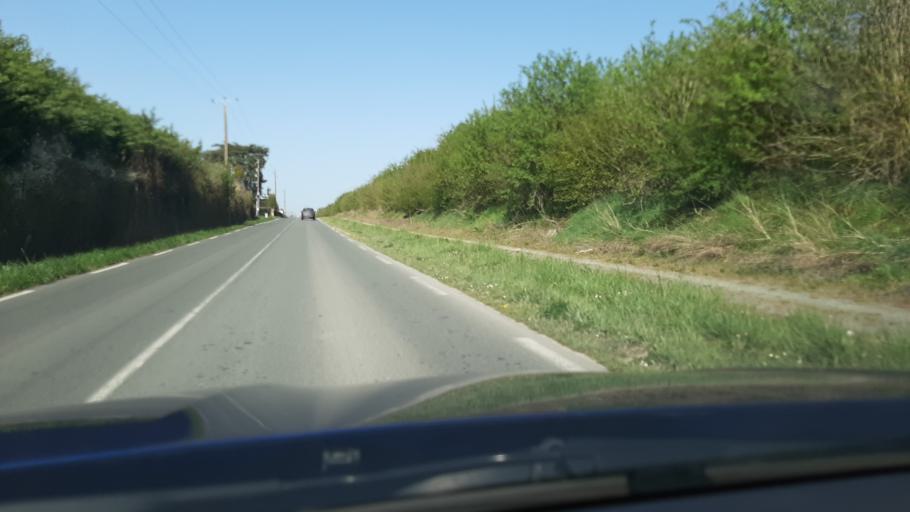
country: FR
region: Pays de la Loire
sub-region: Departement de Maine-et-Loire
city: Pellouailles-les-Vignes
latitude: 47.5123
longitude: -0.4521
